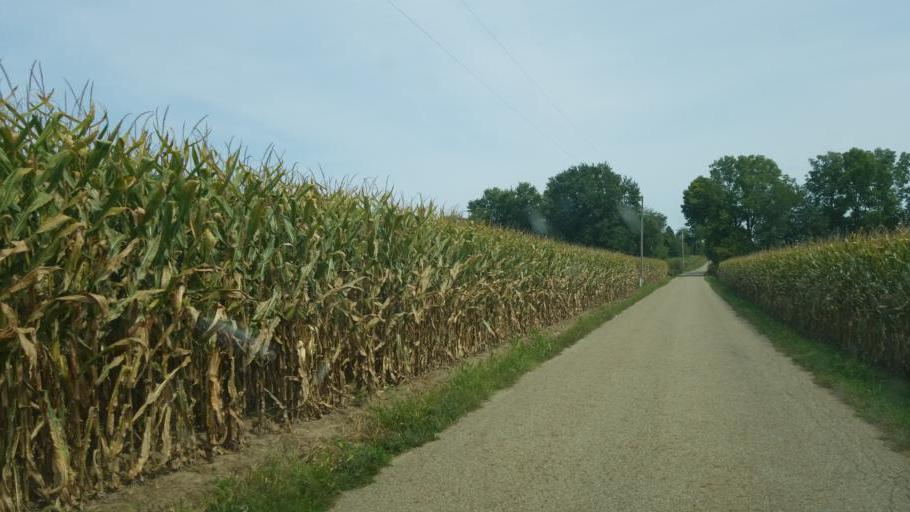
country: US
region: Ohio
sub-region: Knox County
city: Fredericktown
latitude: 40.4708
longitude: -82.5684
